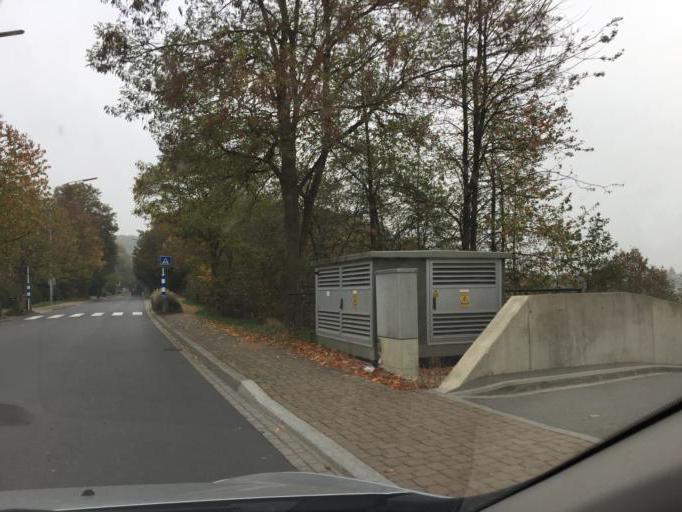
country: LU
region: Luxembourg
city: Moutfort
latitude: 49.5944
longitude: 6.2504
